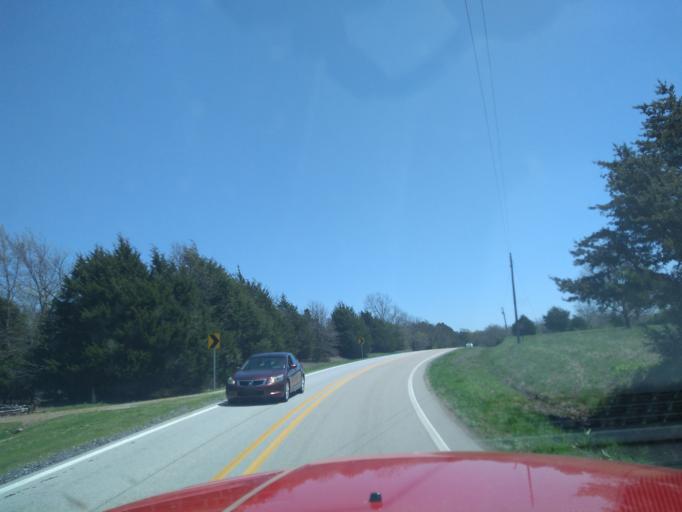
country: US
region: Arkansas
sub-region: Washington County
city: West Fork
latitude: 35.8987
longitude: -94.2413
